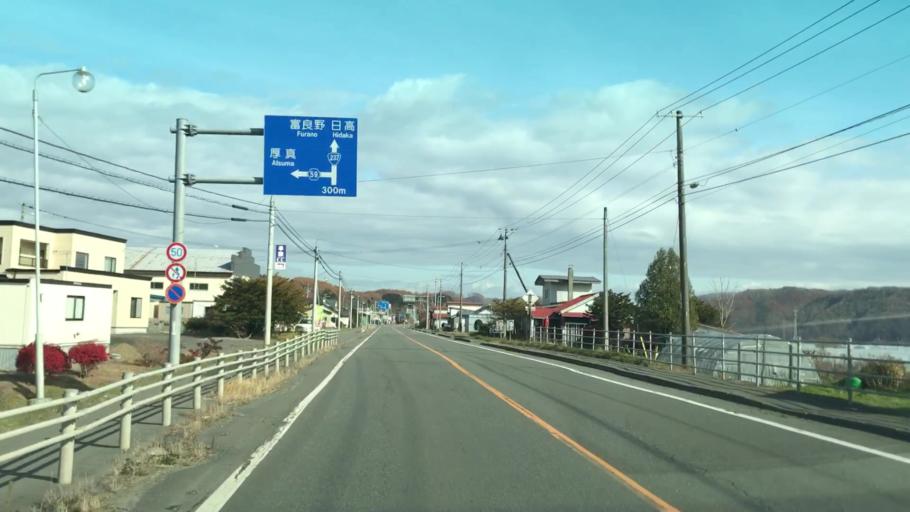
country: JP
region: Hokkaido
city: Shizunai-furukawacho
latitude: 42.5787
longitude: 142.1188
